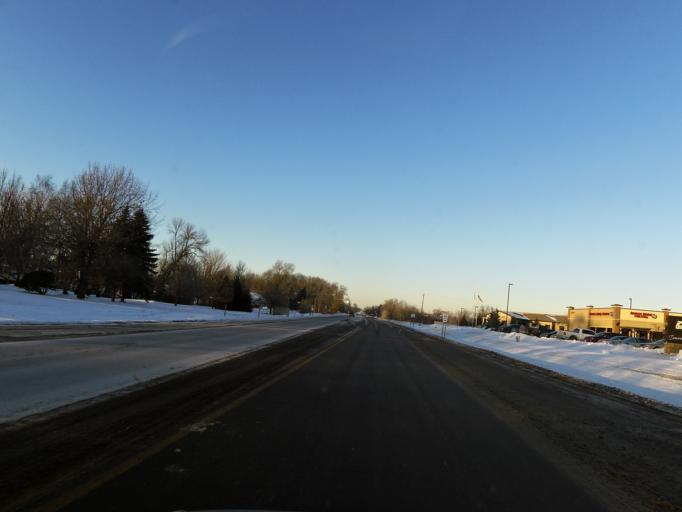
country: US
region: Minnesota
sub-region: Dakota County
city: Farmington
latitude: 44.6474
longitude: -93.1367
